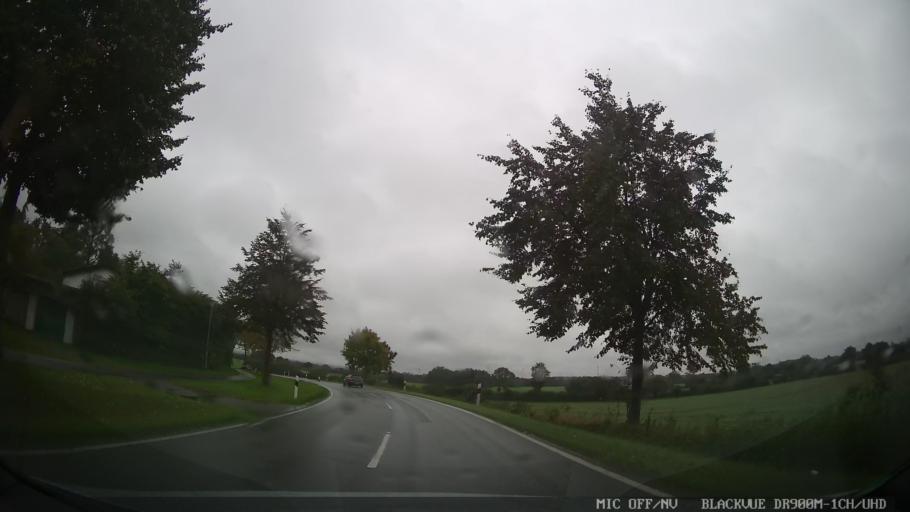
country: DE
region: Schleswig-Holstein
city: Kabelhorst
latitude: 54.2142
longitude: 10.9413
